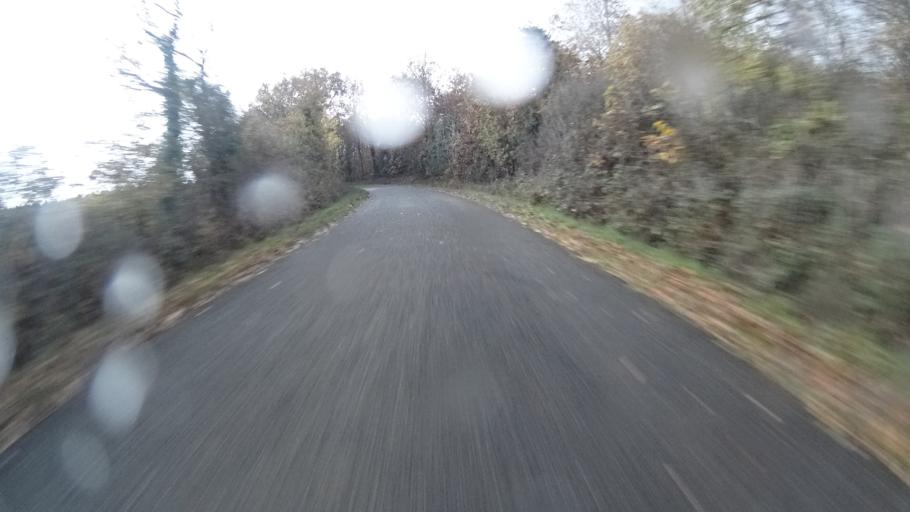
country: FR
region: Pays de la Loire
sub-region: Departement de la Loire-Atlantique
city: Avessac
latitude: 47.6638
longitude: -1.9957
